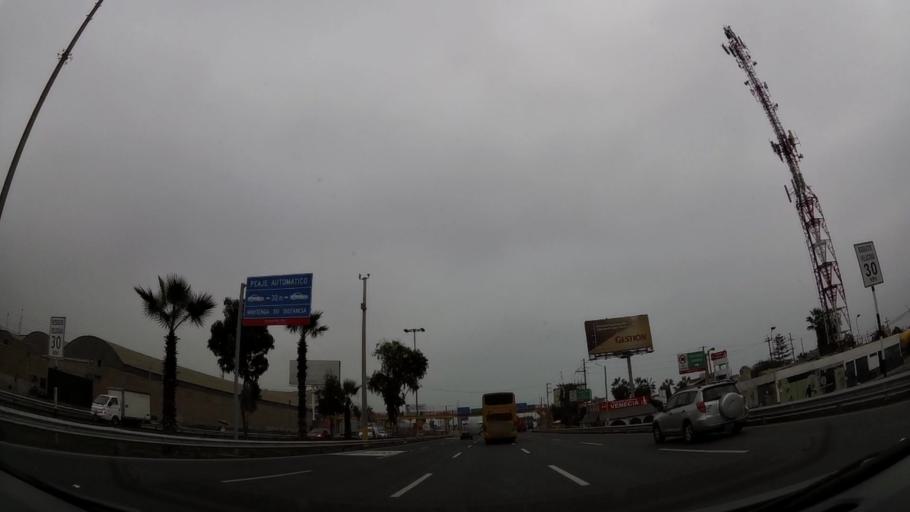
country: PE
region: Lima
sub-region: Lima
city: Surco
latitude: -12.2246
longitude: -76.9727
